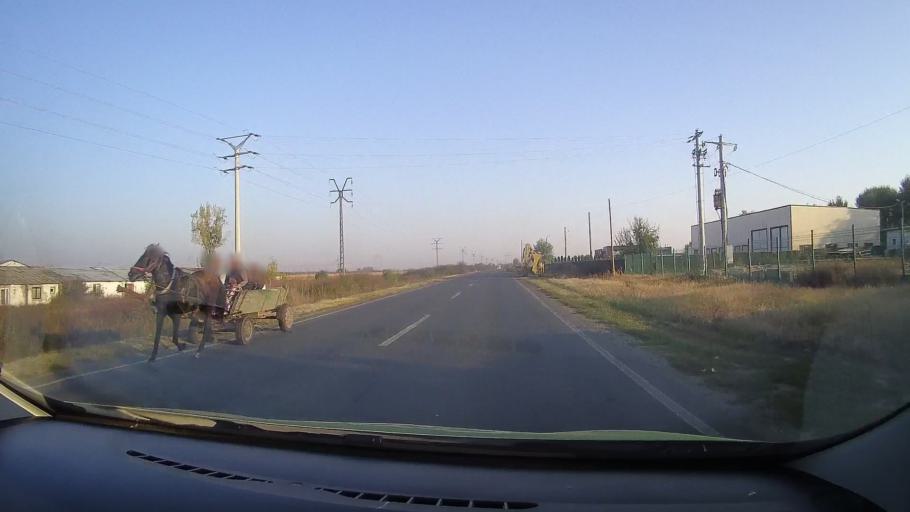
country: RO
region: Arad
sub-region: Comuna Sofronea
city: Sofronea
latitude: 46.2279
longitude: 21.3204
